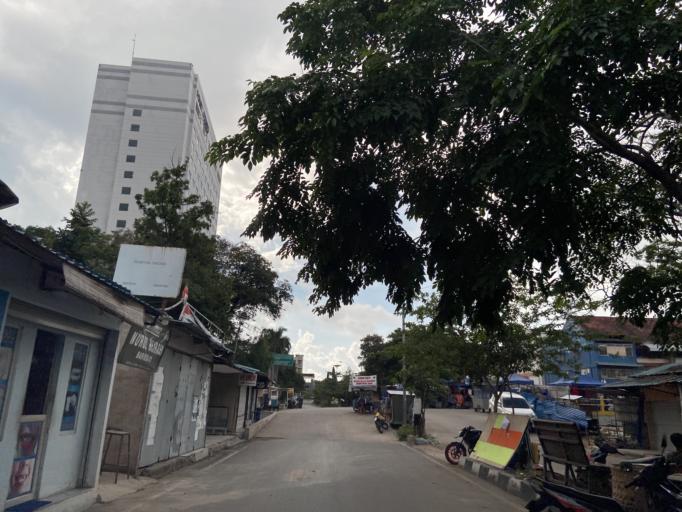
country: SG
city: Singapore
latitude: 1.1484
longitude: 104.0055
